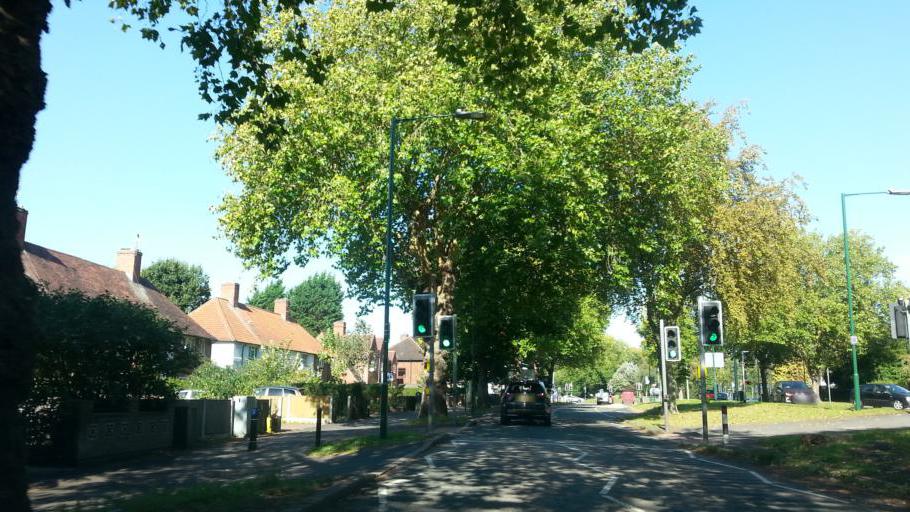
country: GB
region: England
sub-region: Nottingham
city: Nottingham
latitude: 52.9374
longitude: -1.2157
